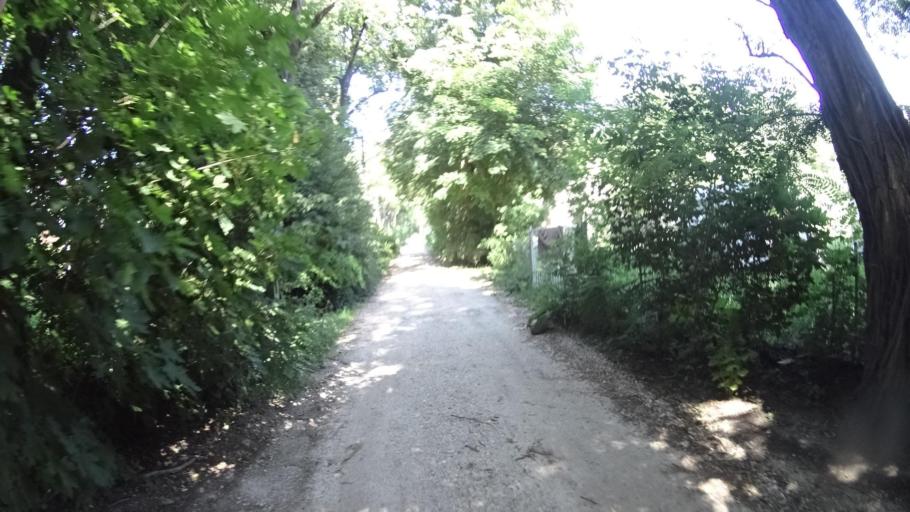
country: PL
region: Masovian Voivodeship
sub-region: Warszawa
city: Bialoleka
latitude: 52.3404
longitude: 20.9773
